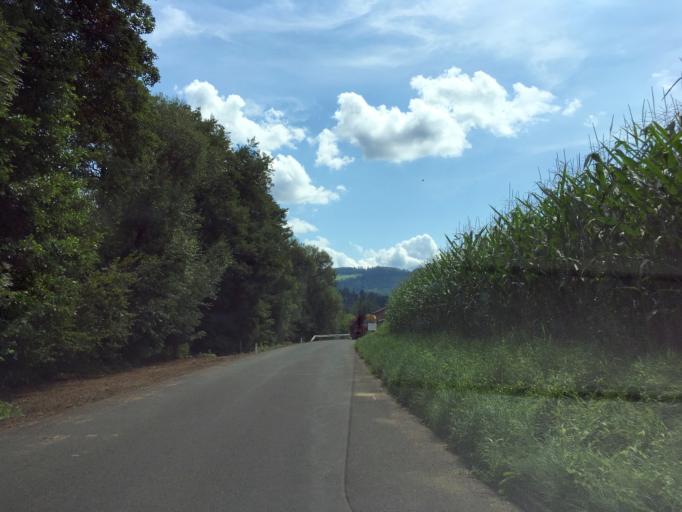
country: AT
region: Styria
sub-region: Politischer Bezirk Leibnitz
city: Oberhaag
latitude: 46.6834
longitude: 15.3523
